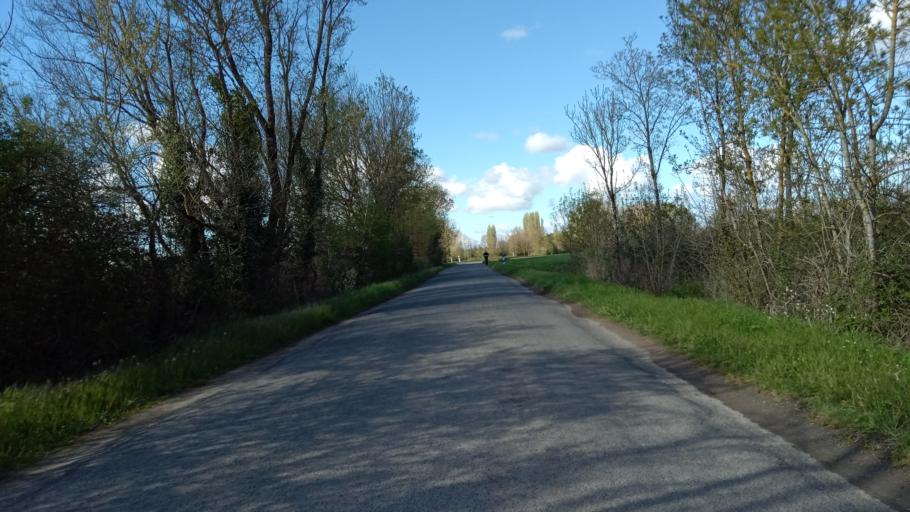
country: FR
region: Poitou-Charentes
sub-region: Departement de la Charente-Maritime
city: Verines
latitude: 46.1487
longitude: -0.9362
